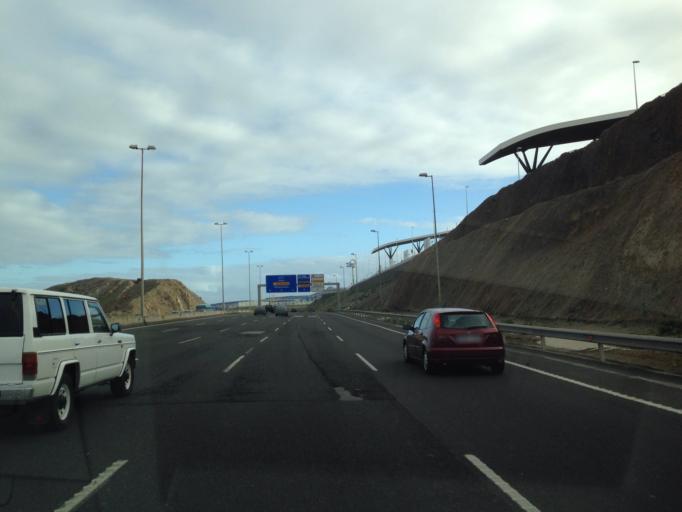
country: ES
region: Canary Islands
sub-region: Provincia de Las Palmas
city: Telde
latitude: 28.0354
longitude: -15.4047
